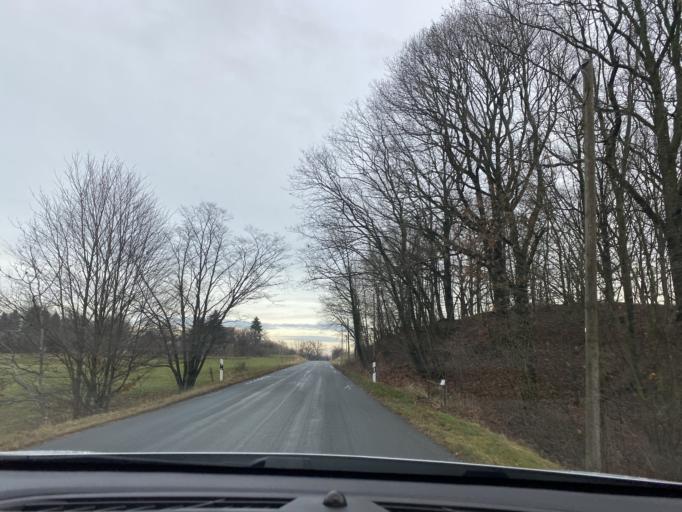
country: DE
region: Saxony
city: Schonau-Berzdorf
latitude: 51.0957
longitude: 14.9065
